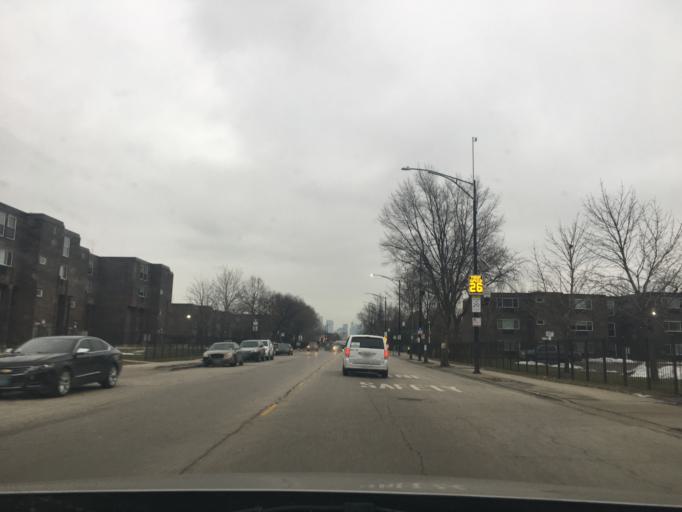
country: US
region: Illinois
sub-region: Cook County
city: Cicero
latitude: 41.8809
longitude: -87.7098
